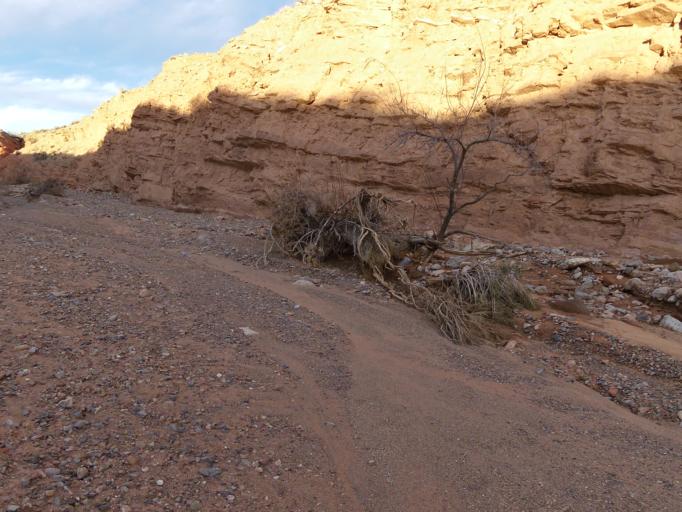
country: US
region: Nevada
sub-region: Clark County
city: Boulder City
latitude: 36.2416
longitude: -114.6324
